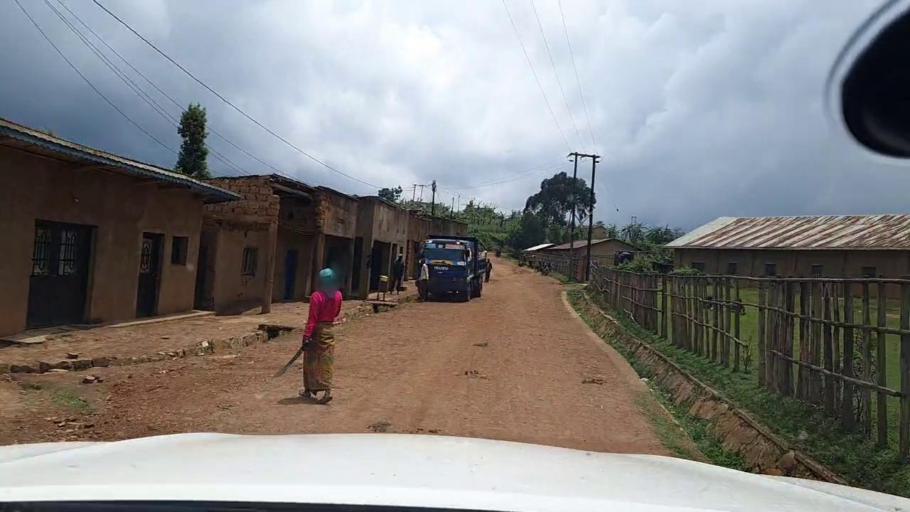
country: RW
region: Western Province
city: Kibuye
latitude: -2.1692
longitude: 29.4299
